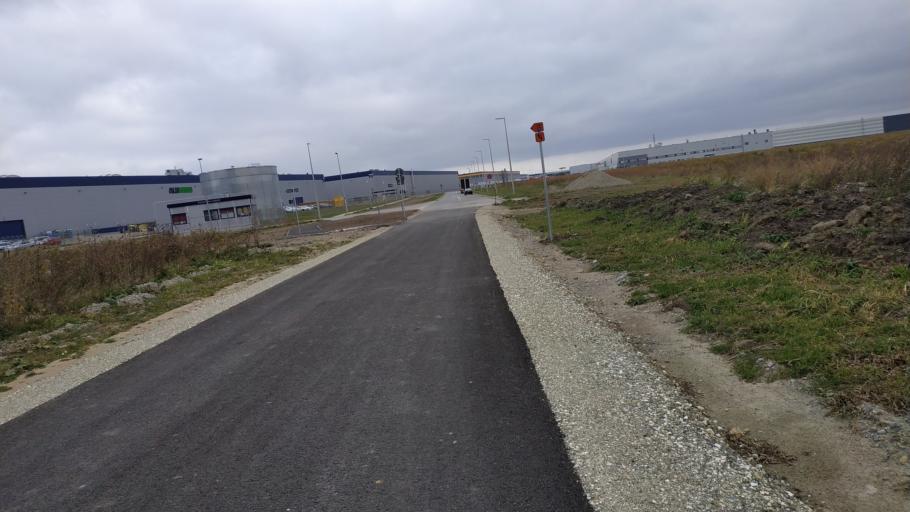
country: PL
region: Lower Silesian Voivodeship
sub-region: Powiat wroclawski
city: Bielany Wroclawskie
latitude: 51.0307
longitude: 16.9501
